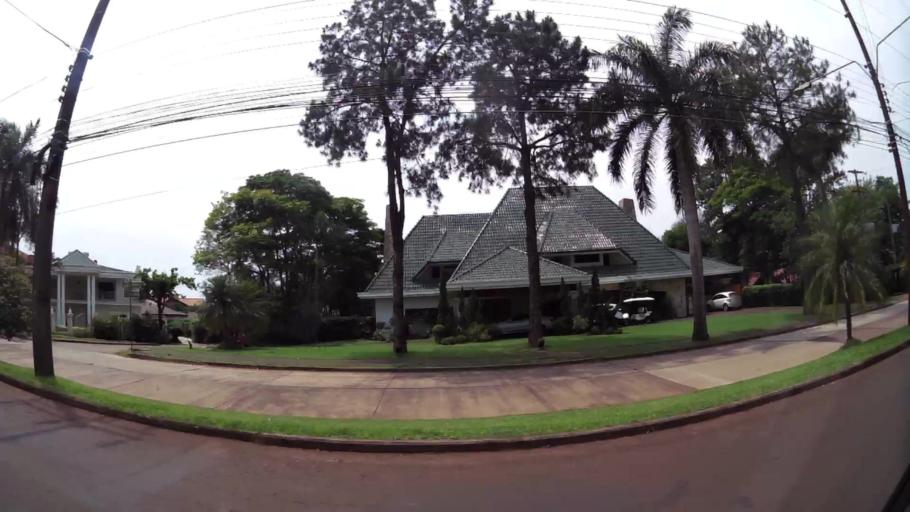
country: PY
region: Alto Parana
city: Ciudad del Este
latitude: -25.4803
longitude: -54.6201
